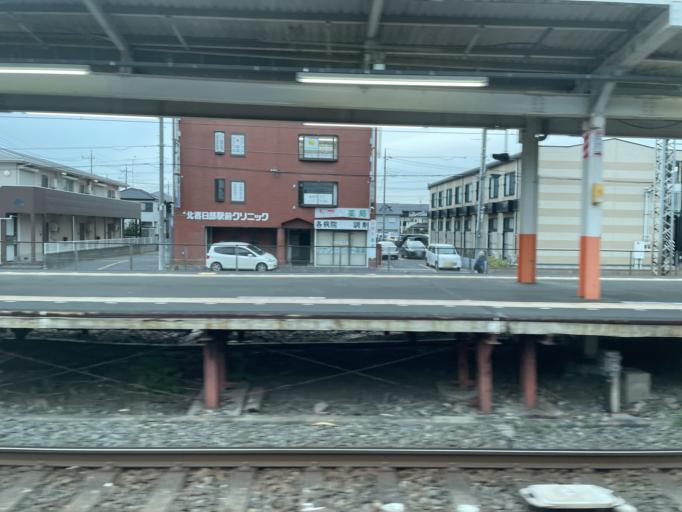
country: JP
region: Saitama
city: Kasukabe
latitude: 35.9894
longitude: 139.7445
